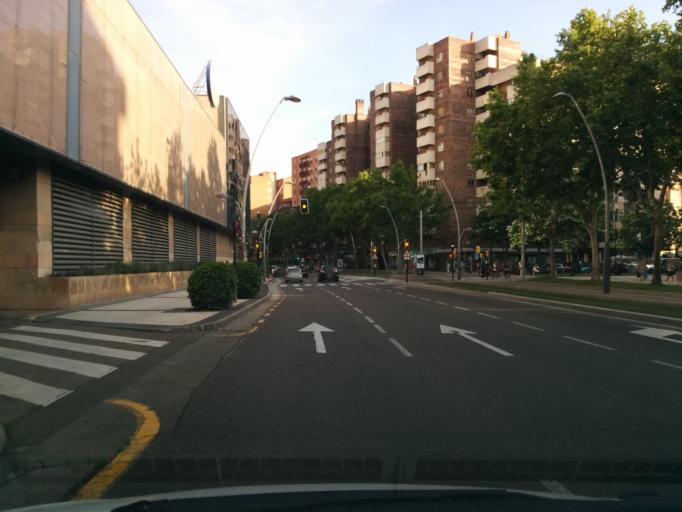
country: ES
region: Aragon
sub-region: Provincia de Zaragoza
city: Almozara
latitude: 41.6711
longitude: -0.8907
